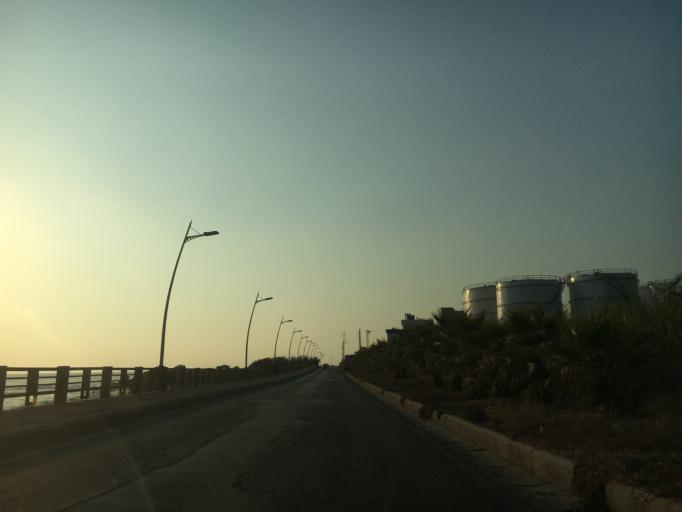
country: LB
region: Mont-Liban
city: Jbail
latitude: 34.1401
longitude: 35.6317
